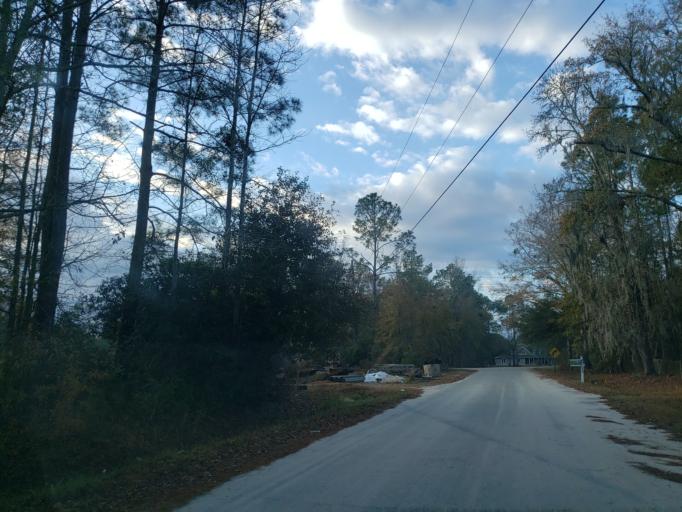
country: US
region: Georgia
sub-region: Chatham County
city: Bloomingdale
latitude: 32.1320
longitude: -81.3109
